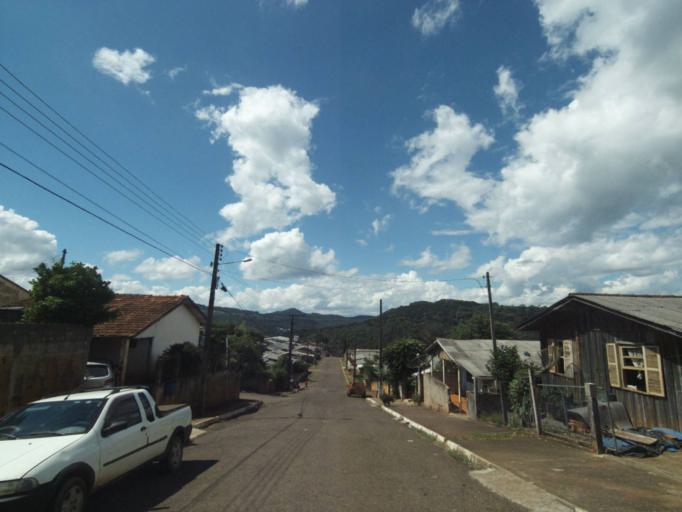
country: BR
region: Parana
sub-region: Uniao Da Vitoria
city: Uniao da Vitoria
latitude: -26.1741
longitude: -51.5514
